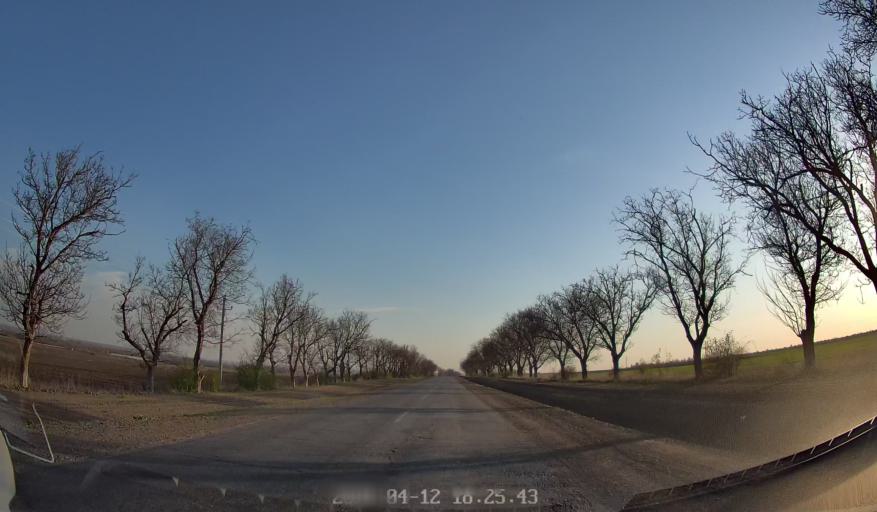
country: MD
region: Criuleni
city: Criuleni
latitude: 47.1807
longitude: 29.1369
